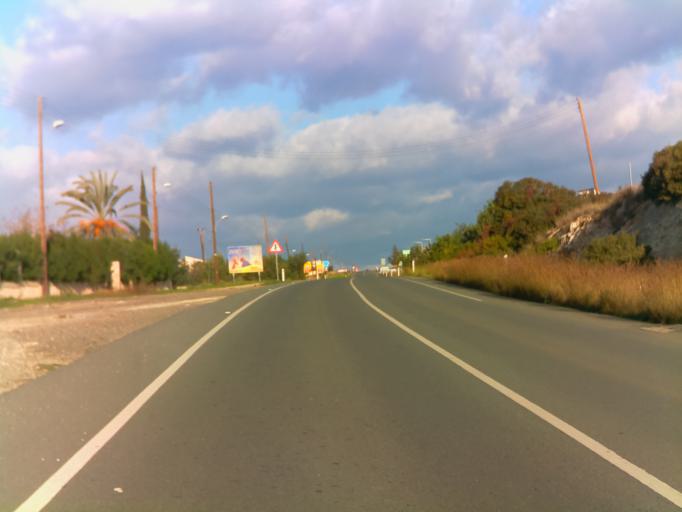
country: CY
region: Pafos
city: Pegeia
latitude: 34.8720
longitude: 32.3604
